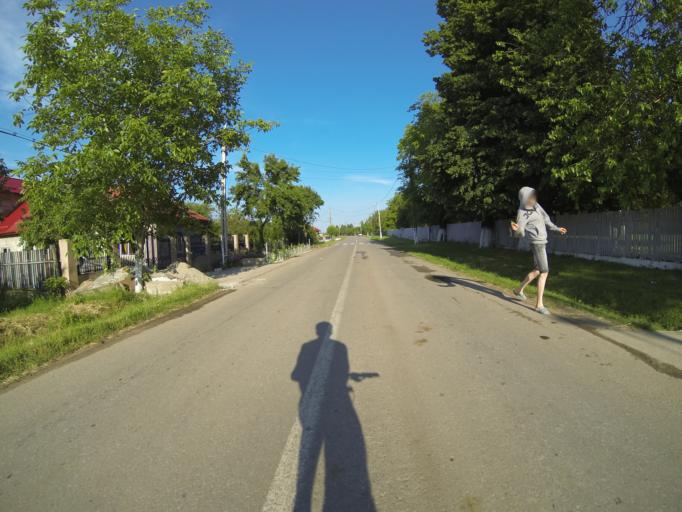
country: RO
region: Dolj
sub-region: Comuna Caloparu
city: Calopar
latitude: 44.1626
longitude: 23.7643
